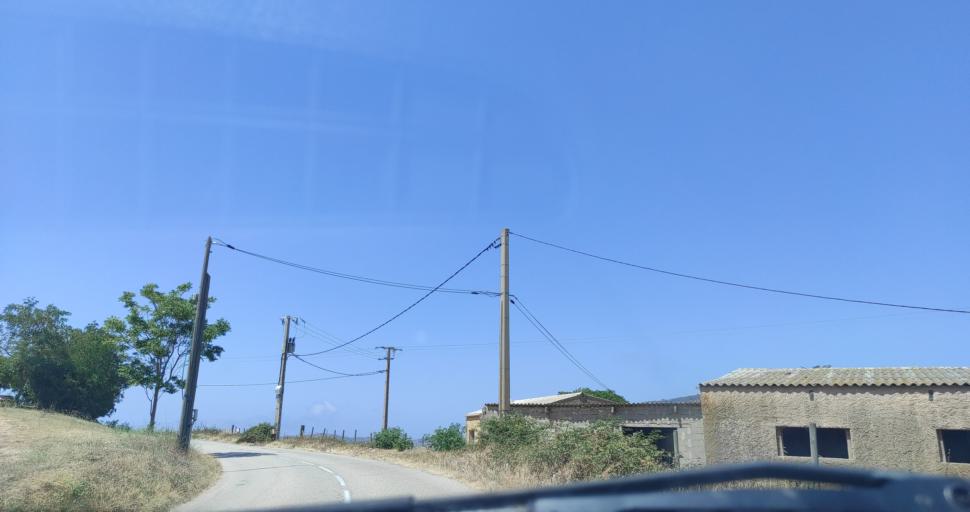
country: FR
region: Corsica
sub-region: Departement de la Corse-du-Sud
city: Alata
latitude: 41.9671
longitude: 8.7129
